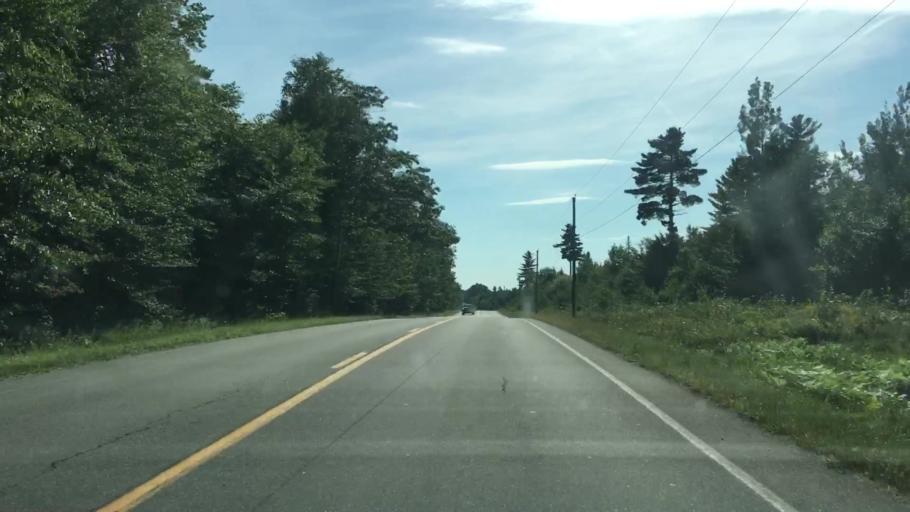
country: US
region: Maine
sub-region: Penobscot County
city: Lincoln
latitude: 45.3746
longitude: -68.5532
